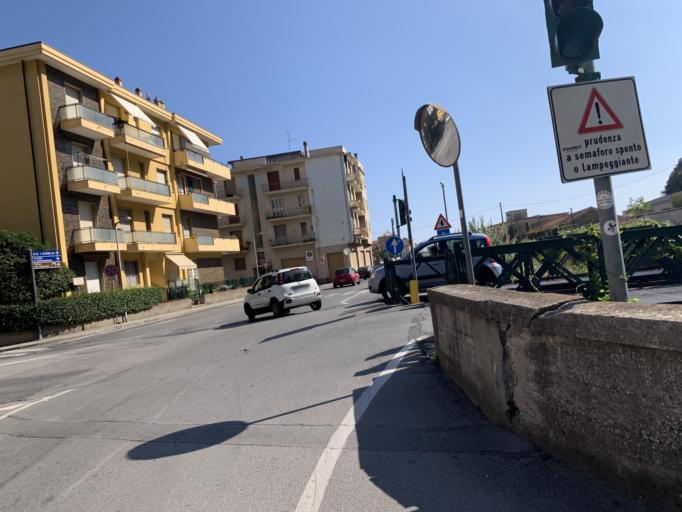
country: IT
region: Liguria
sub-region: Provincia di Savona
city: Finale Ligure
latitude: 44.1708
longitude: 8.3350
